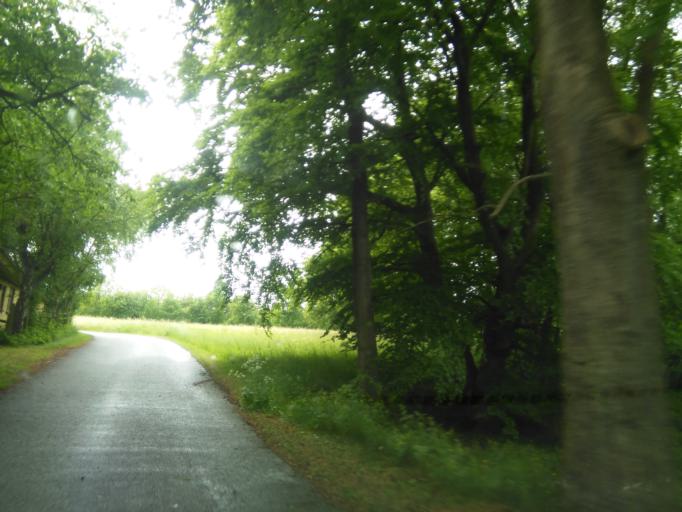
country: DK
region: Capital Region
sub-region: Bornholm Kommune
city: Nexo
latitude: 55.0975
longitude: 15.1183
